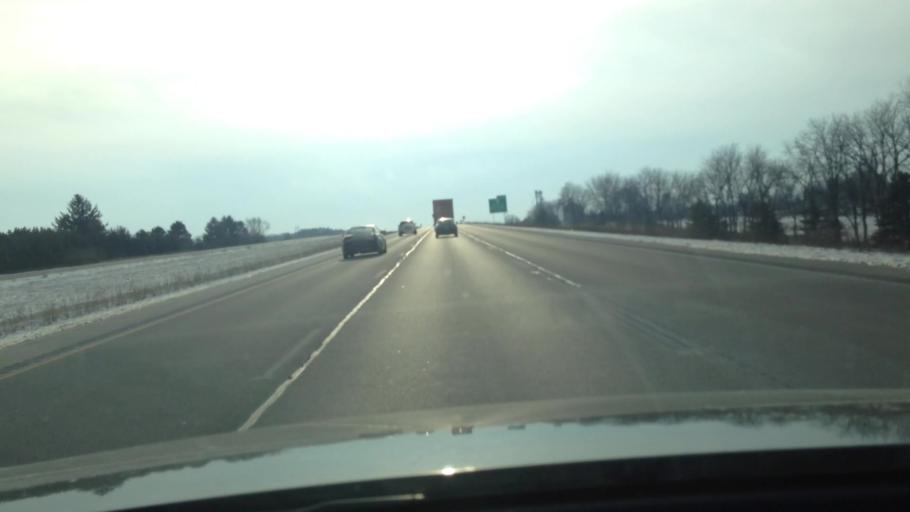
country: US
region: Wisconsin
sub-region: Walworth County
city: Elkhorn
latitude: 42.7096
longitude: -88.4812
